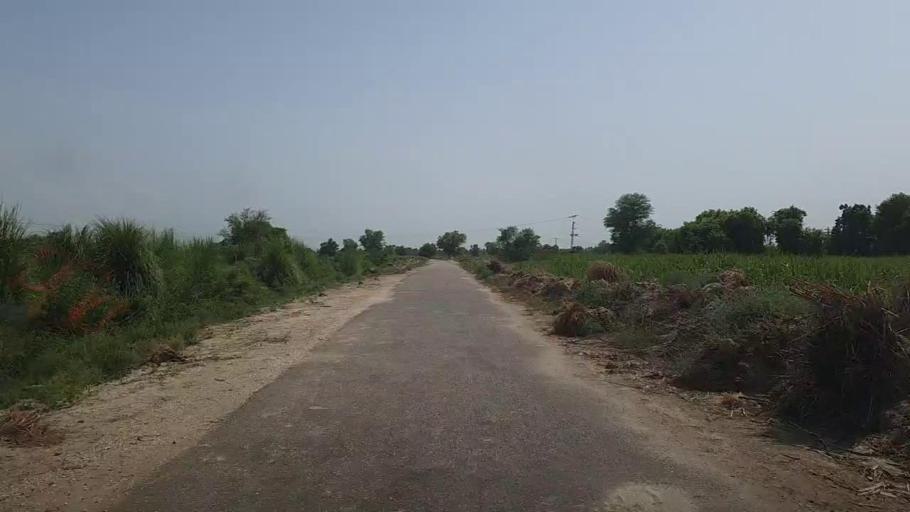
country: PK
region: Sindh
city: Pad Idan
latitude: 26.8266
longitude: 68.3289
